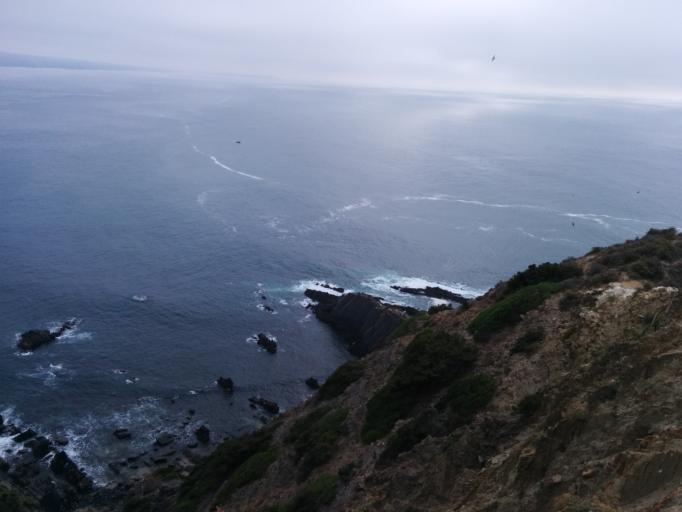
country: PT
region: Faro
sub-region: Aljezur
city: Aljezur
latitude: 37.2963
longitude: -8.8742
